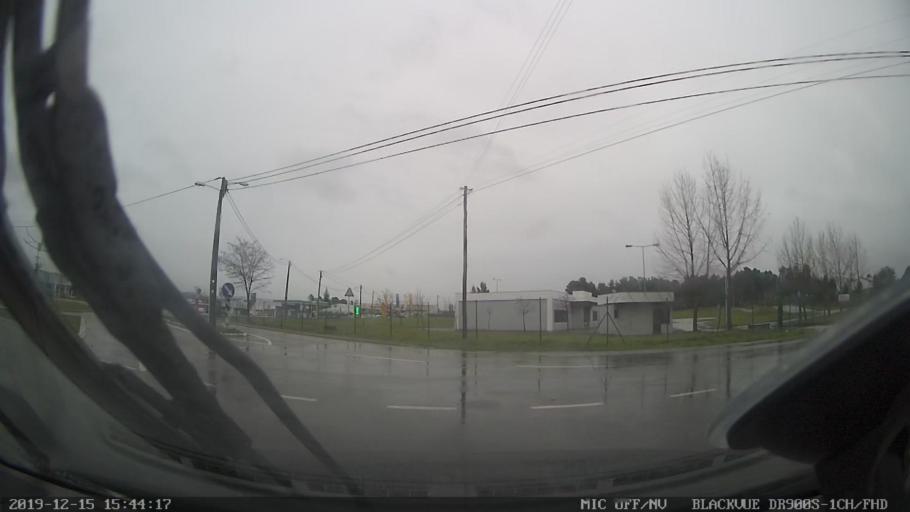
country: PT
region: Vila Real
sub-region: Vila Real
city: Vila Real
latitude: 41.2764
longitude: -7.7202
